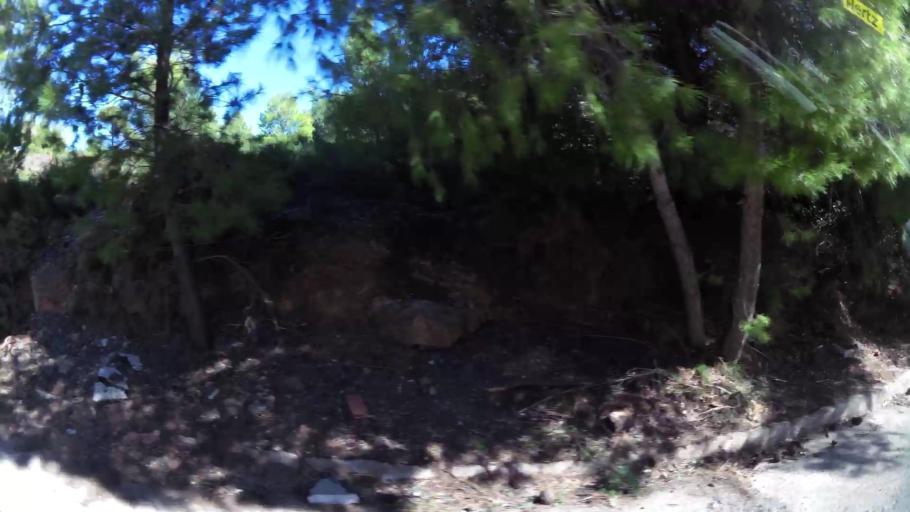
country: GR
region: Attica
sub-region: Nomarchia Anatolikis Attikis
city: Dioni
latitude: 38.0279
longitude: 23.9352
